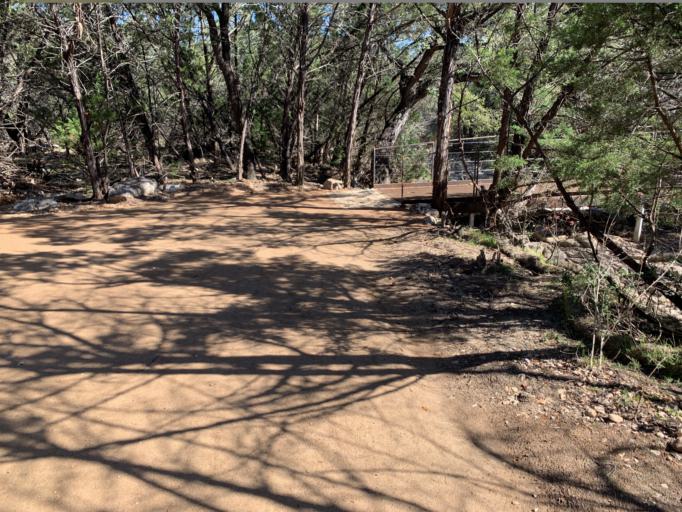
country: US
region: Texas
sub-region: Travis County
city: Shady Hollow
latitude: 30.1955
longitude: -97.8665
